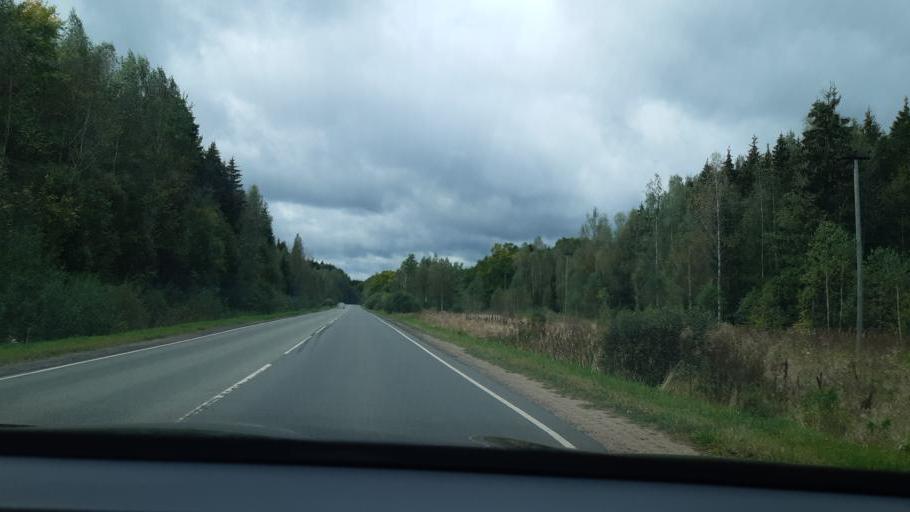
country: RU
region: Moskovskaya
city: Melikhovo
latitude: 55.1220
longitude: 37.6276
